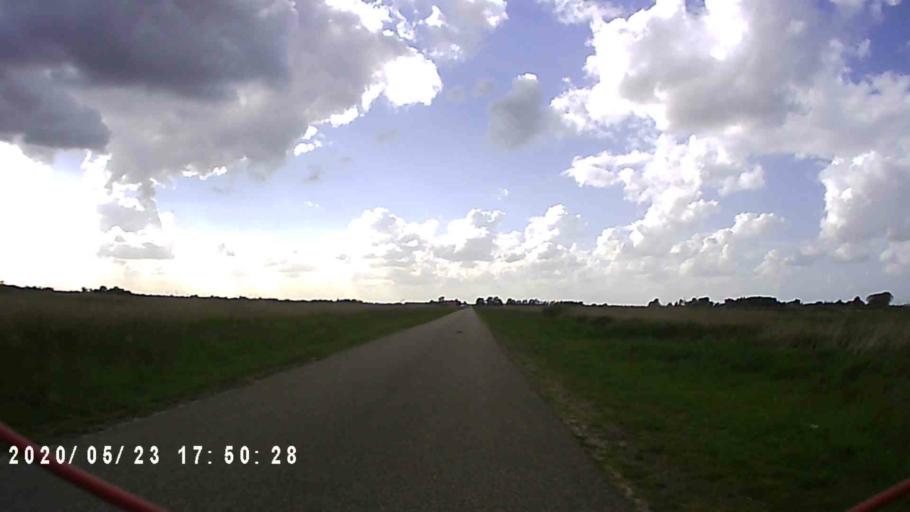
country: NL
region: Groningen
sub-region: Gemeente Slochteren
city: Slochteren
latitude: 53.2394
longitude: 6.7649
